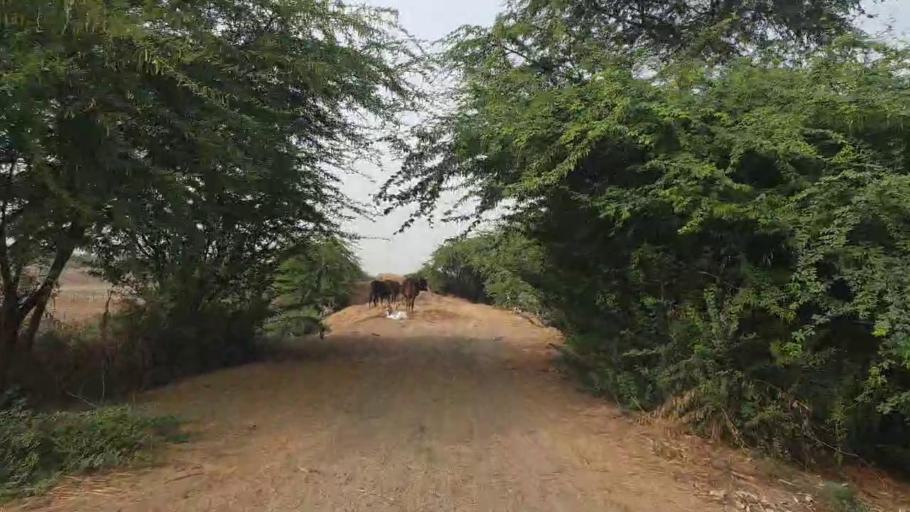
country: PK
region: Sindh
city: Mirpur Batoro
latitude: 24.6240
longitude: 68.3994
